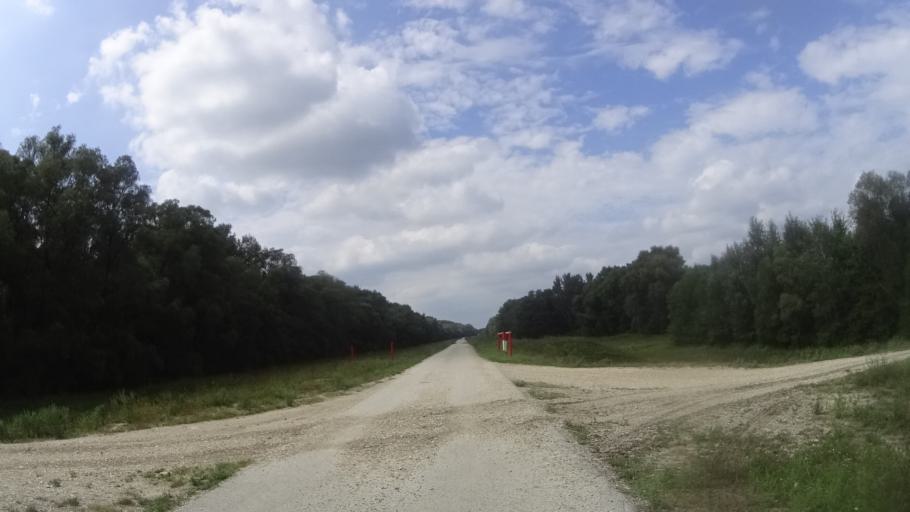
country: SK
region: Trnavsky
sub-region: Okres Dunajska Streda
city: Velky Meder
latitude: 47.7722
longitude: 17.7139
